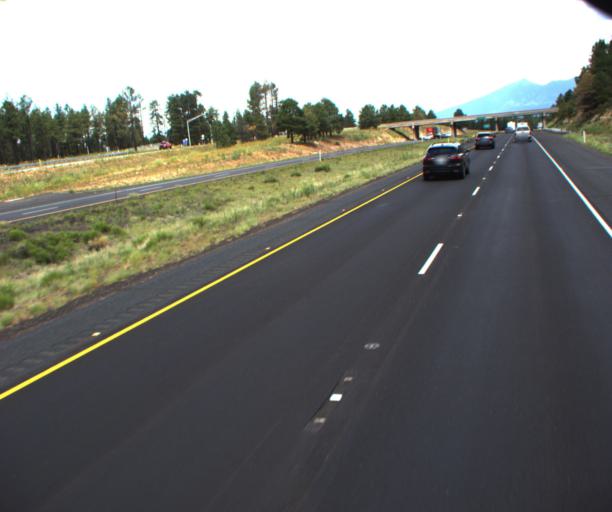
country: US
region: Arizona
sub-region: Coconino County
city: Kachina Village
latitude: 35.1378
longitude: -111.6846
